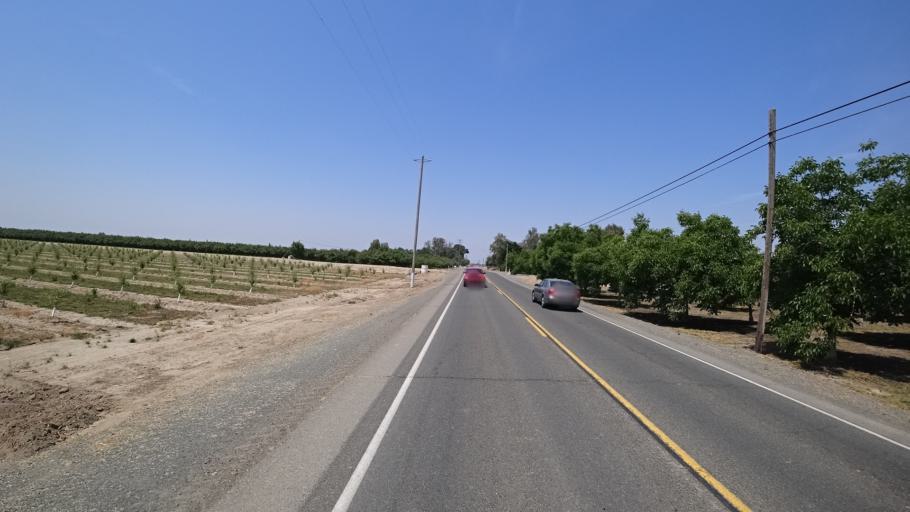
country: US
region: California
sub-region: Kings County
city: Armona
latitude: 36.3280
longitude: -119.7369
